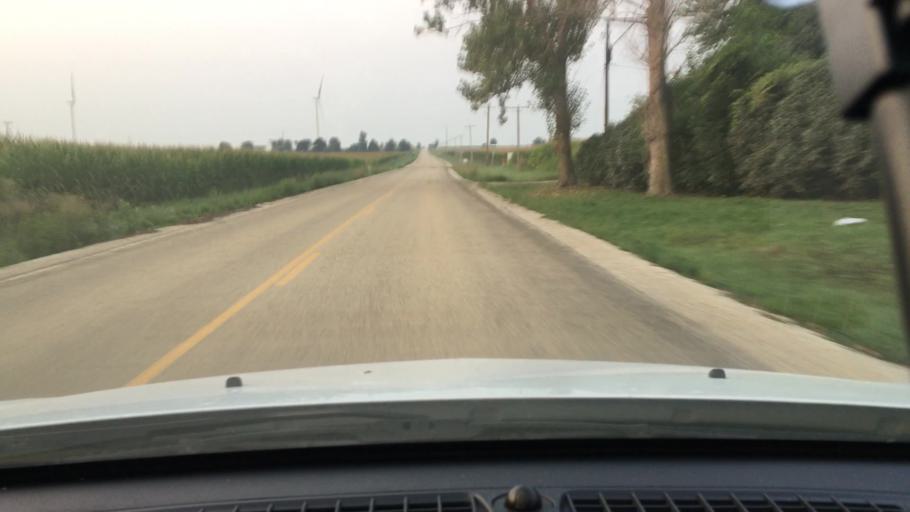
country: US
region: Illinois
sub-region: DeKalb County
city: Waterman
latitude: 41.8357
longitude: -88.7733
